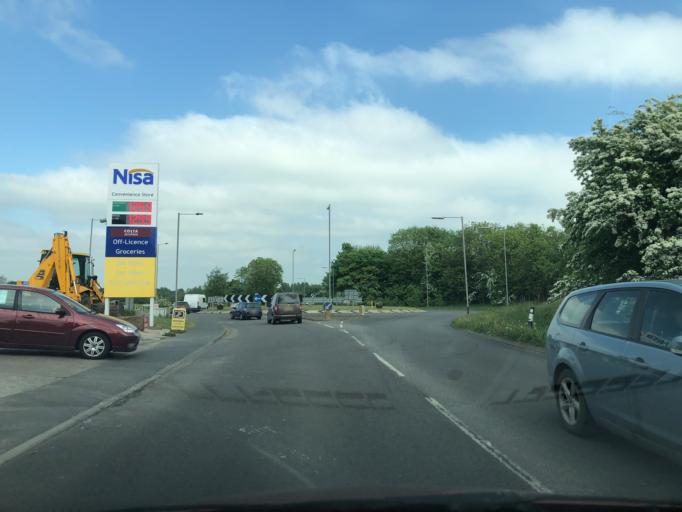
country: GB
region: England
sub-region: North Yorkshire
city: Catterick Garrison
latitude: 54.3799
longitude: -1.6783
